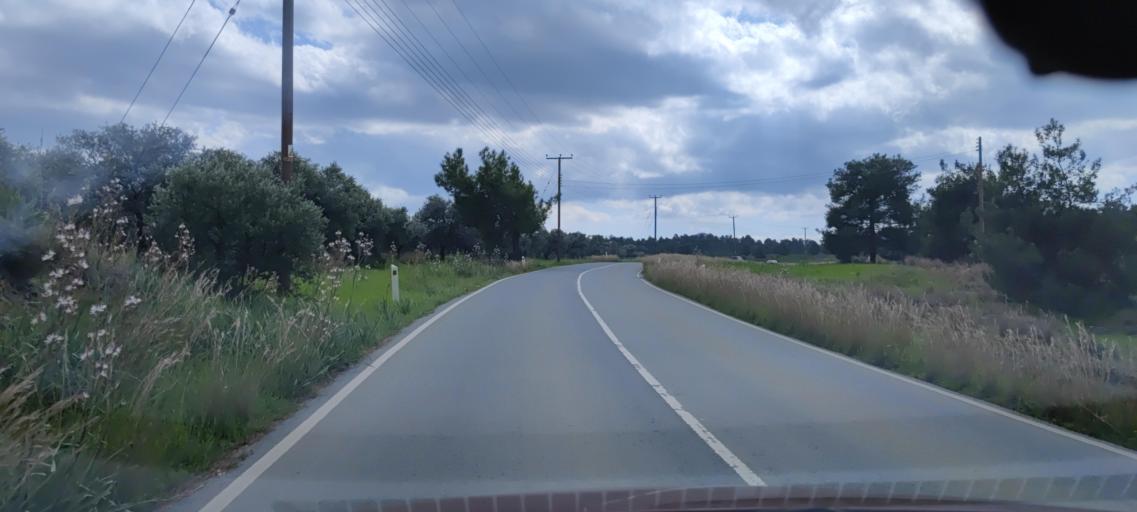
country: CY
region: Lefkosia
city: Lythrodontas
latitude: 34.9768
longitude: 33.2962
